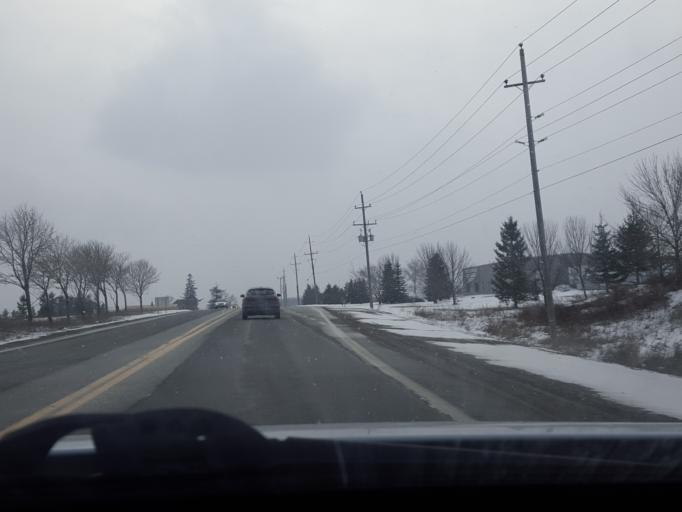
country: CA
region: Ontario
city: Uxbridge
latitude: 44.0188
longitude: -79.2296
